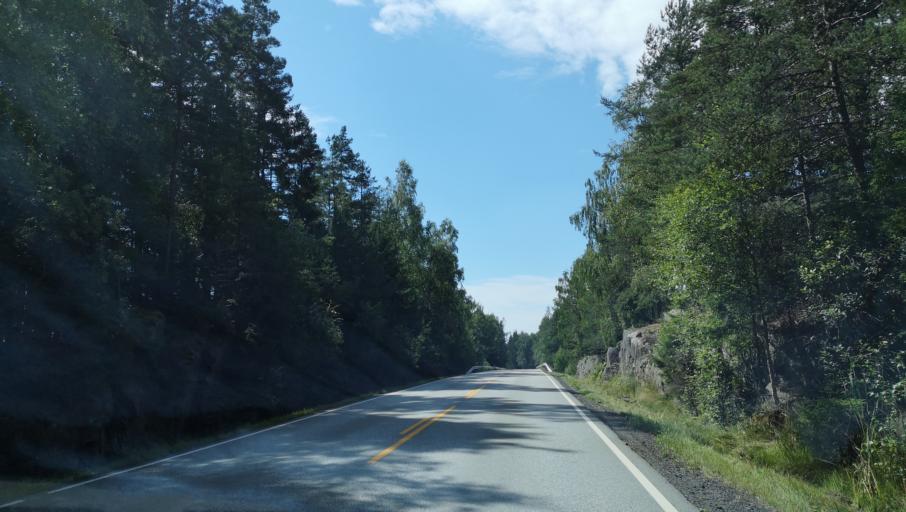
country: NO
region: Akershus
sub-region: Vestby
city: Vestby
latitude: 59.5363
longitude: 10.7622
